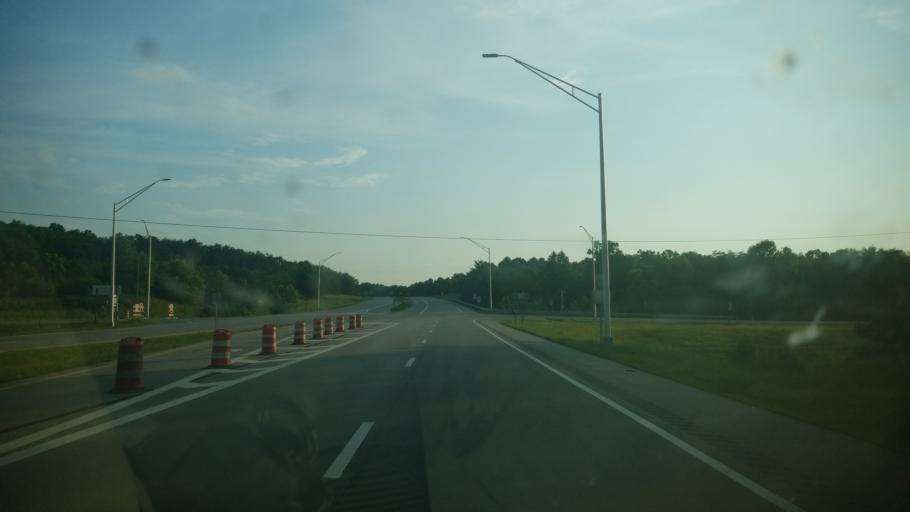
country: US
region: Ohio
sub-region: Adams County
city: Peebles
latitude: 38.9755
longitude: -83.3385
